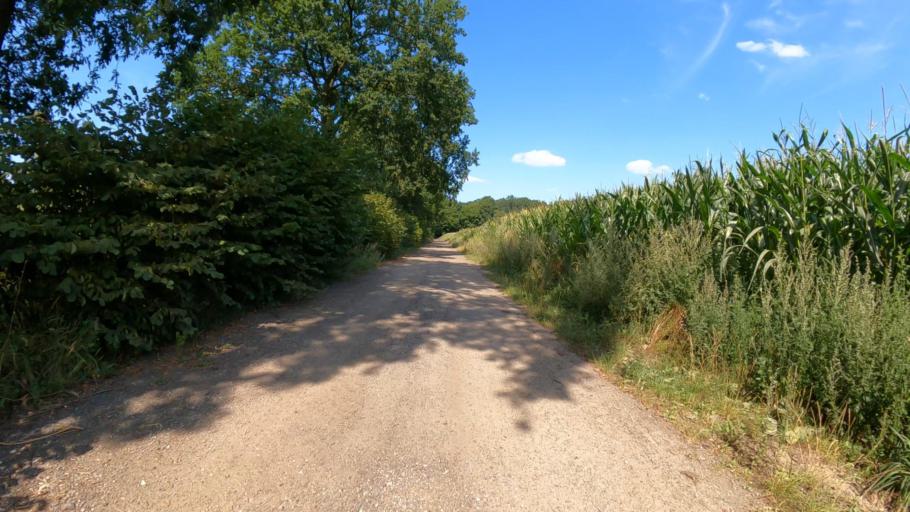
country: DE
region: Schleswig-Holstein
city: Ellerhoop
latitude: 53.7332
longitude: 9.7658
